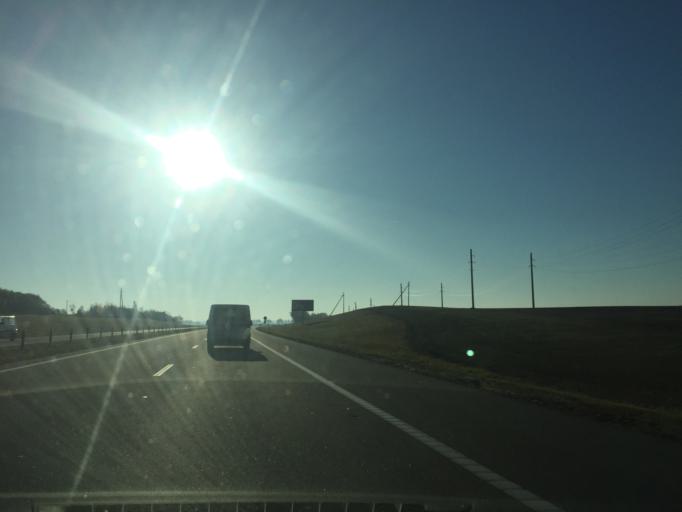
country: BY
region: Minsk
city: Luhavaya Slabada
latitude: 53.7757
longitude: 27.8535
